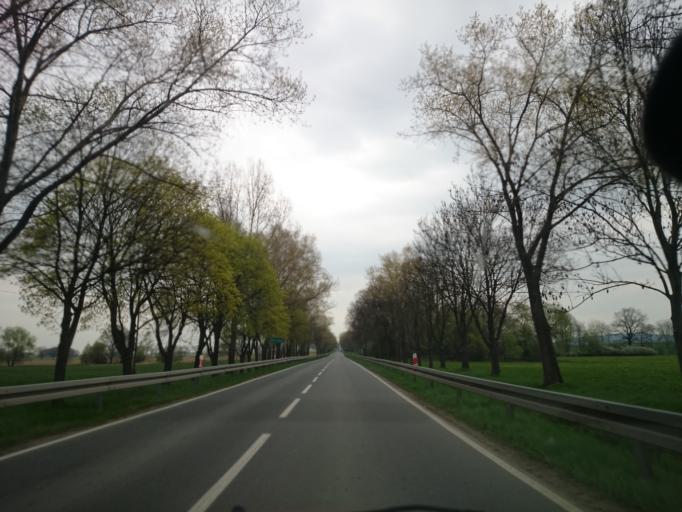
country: PL
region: Opole Voivodeship
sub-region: Powiat prudnicki
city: Moszczanka
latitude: 50.3269
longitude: 17.4815
